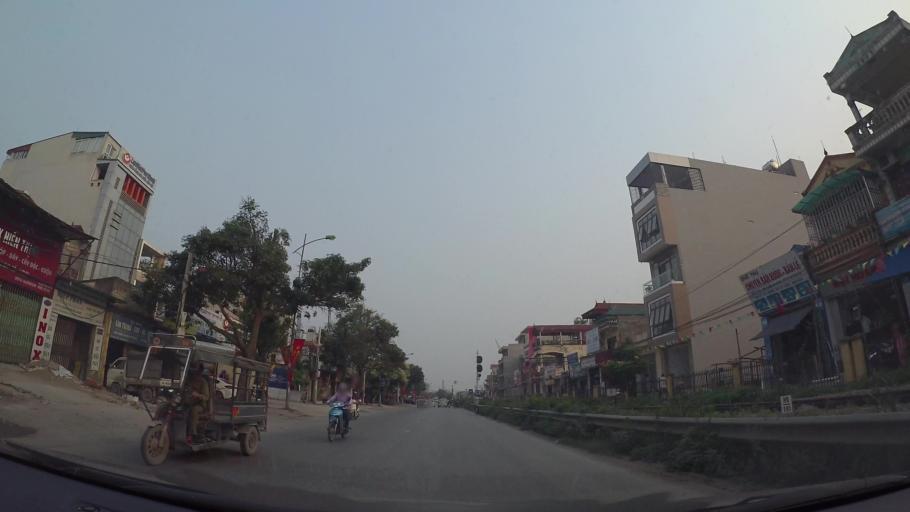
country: VN
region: Ha Noi
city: Thuong Tin
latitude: 20.8756
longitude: 105.8627
